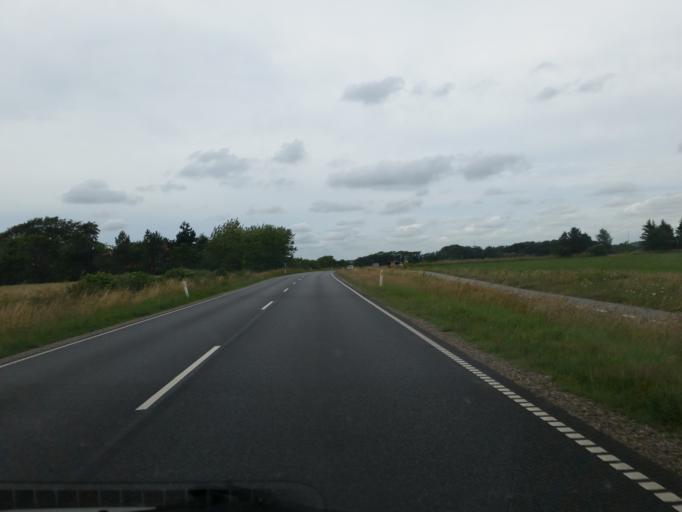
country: DK
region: South Denmark
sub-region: Esbjerg Kommune
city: Ribe
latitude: 55.2610
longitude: 8.7223
